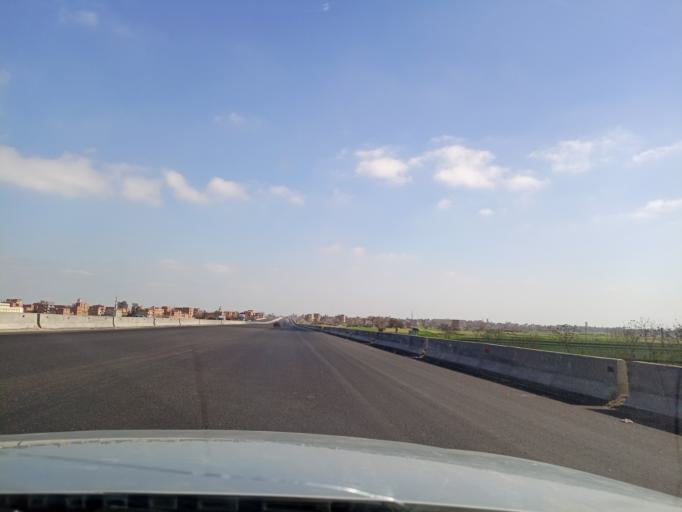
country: EG
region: Muhafazat al Minufiyah
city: Al Bajur
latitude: 30.4125
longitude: 31.0610
